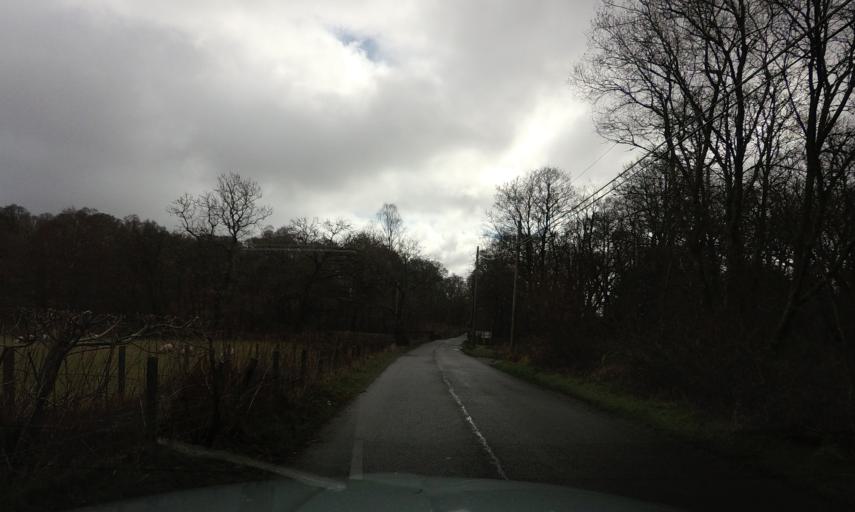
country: GB
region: Scotland
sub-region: West Dunbartonshire
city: Balloch
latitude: 56.1026
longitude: -4.5646
